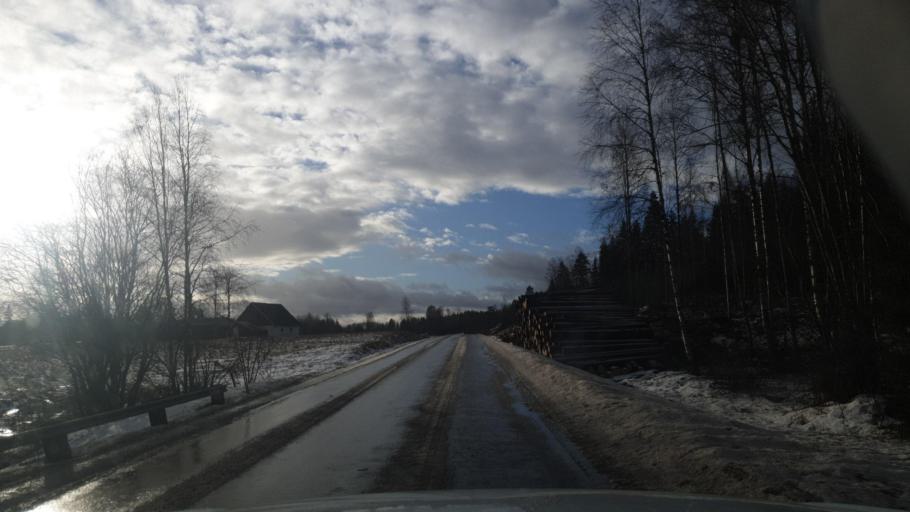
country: SE
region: Vaermland
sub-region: Eda Kommun
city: Charlottenberg
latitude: 59.7978
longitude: 12.1541
